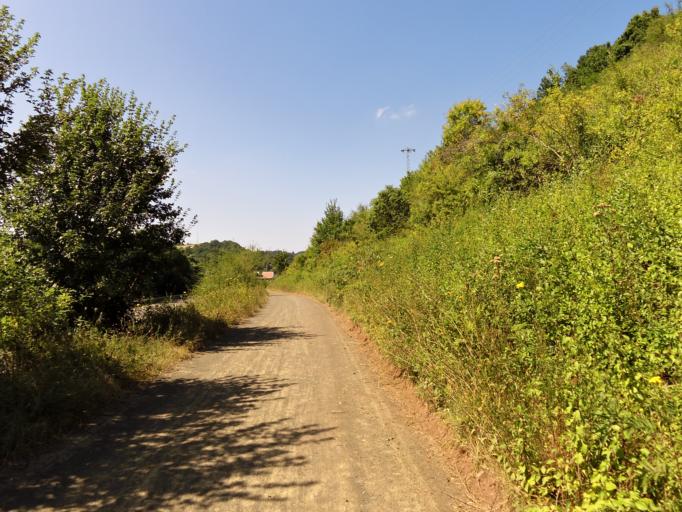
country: DE
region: Rheinland-Pfalz
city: Winnweiler
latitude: 49.5693
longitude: 7.8605
